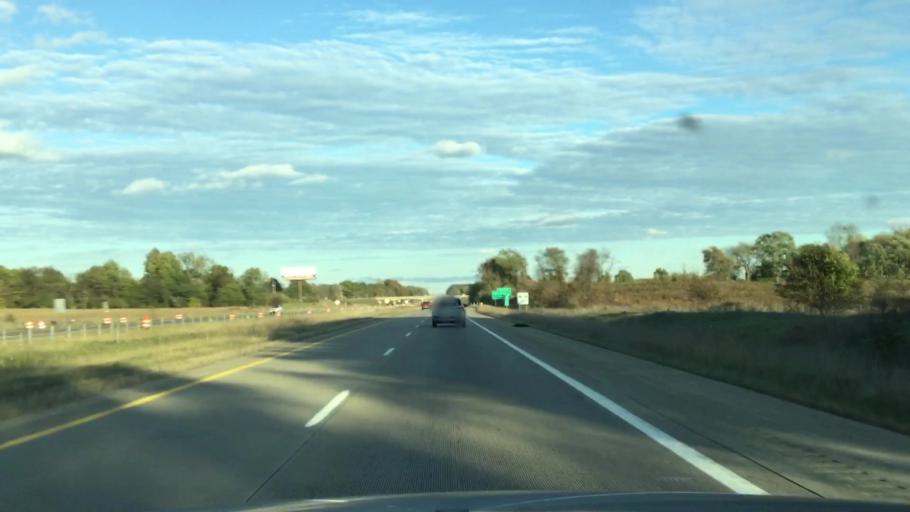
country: US
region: Michigan
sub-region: Calhoun County
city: Marshall
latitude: 42.2829
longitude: -84.8717
